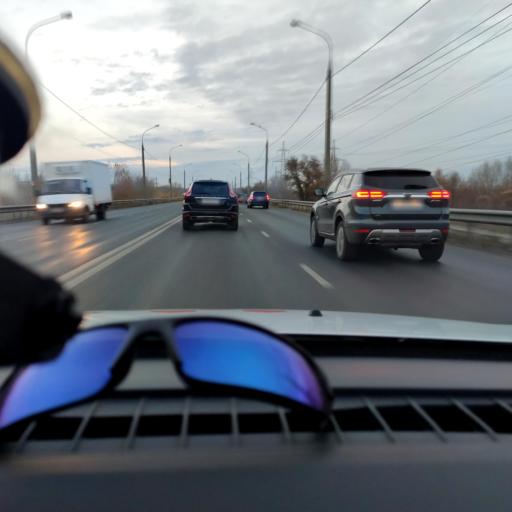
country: RU
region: Samara
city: Samara
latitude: 53.1555
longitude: 50.1901
